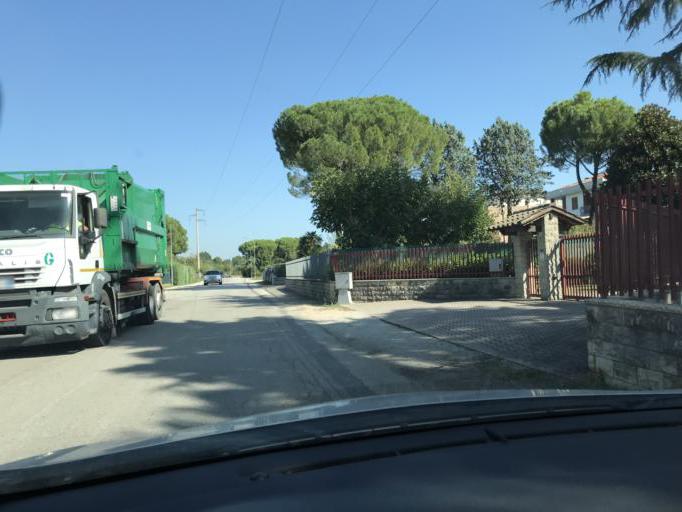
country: IT
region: Umbria
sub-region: Provincia di Perugia
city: Ponte Felcino
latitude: 43.1092
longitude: 12.4534
